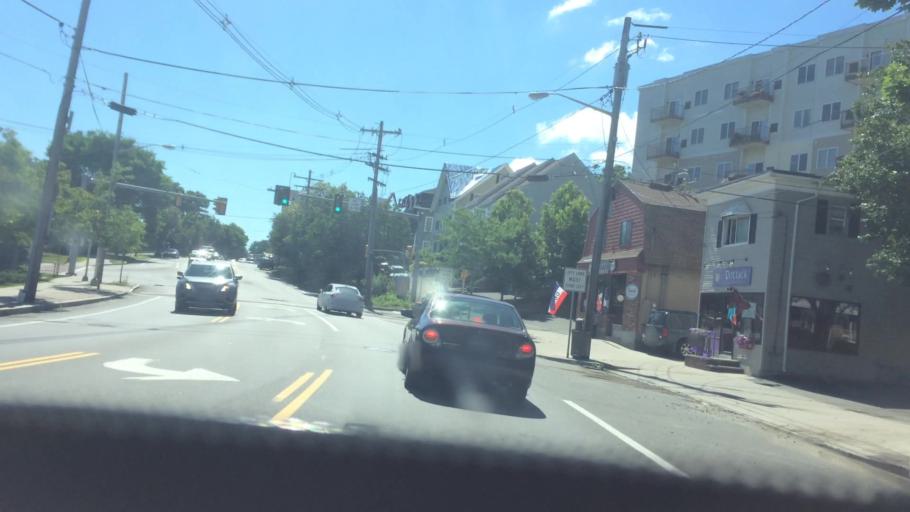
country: US
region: Massachusetts
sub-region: Essex County
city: Peabody
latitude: 42.5230
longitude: -70.9203
